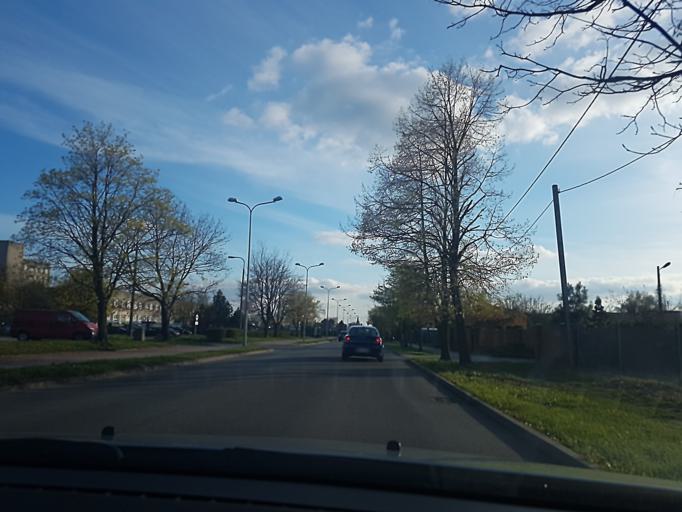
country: PL
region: Lodz Voivodeship
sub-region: Powiat kutnowski
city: Kutno
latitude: 52.2406
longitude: 19.3723
